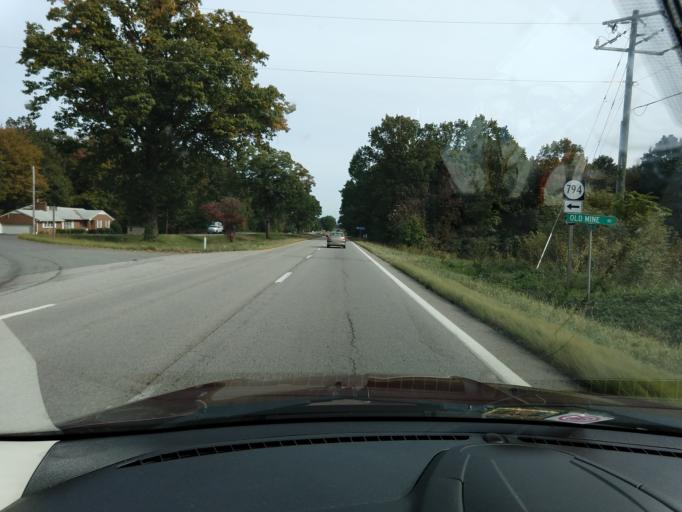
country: US
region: Virginia
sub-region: Pittsylvania County
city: Chatham
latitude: 36.8892
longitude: -79.4025
